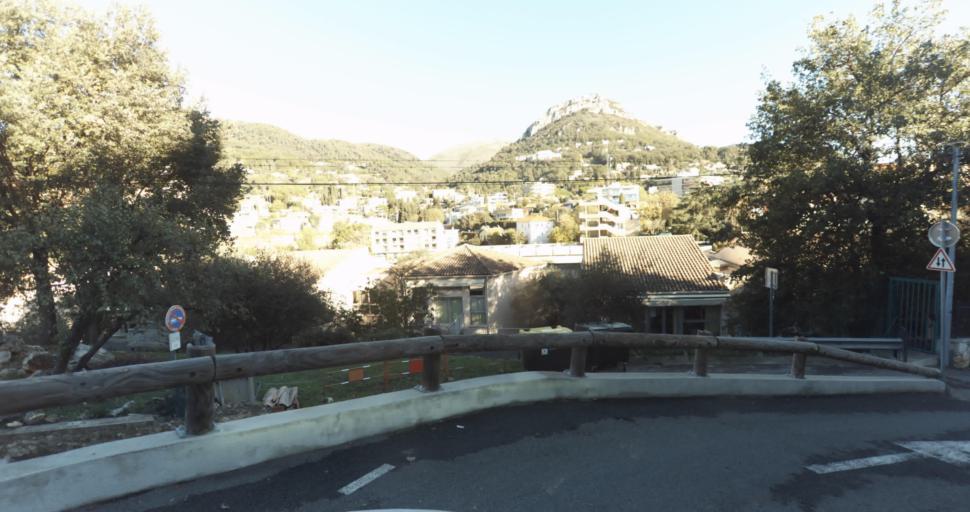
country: FR
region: Provence-Alpes-Cote d'Azur
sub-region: Departement des Alpes-Maritimes
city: Vence
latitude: 43.7227
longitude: 7.1030
